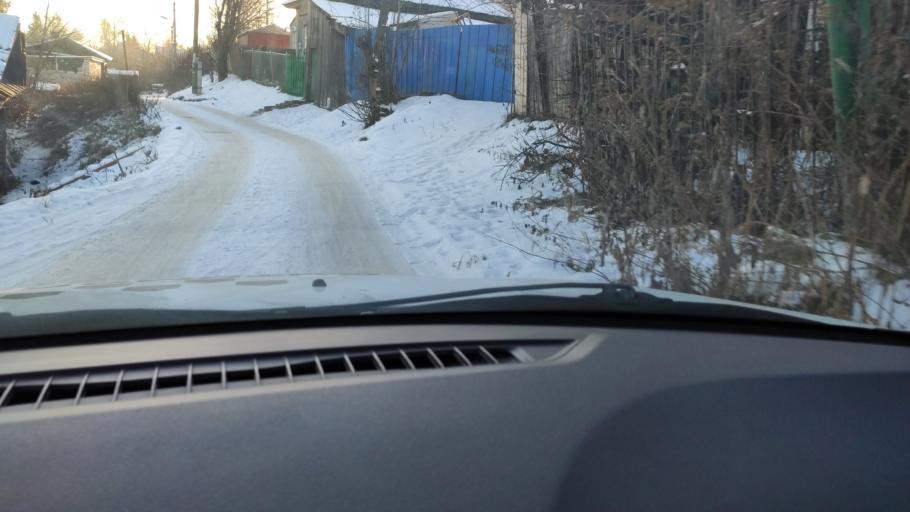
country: RU
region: Perm
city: Perm
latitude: 58.0332
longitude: 56.3318
